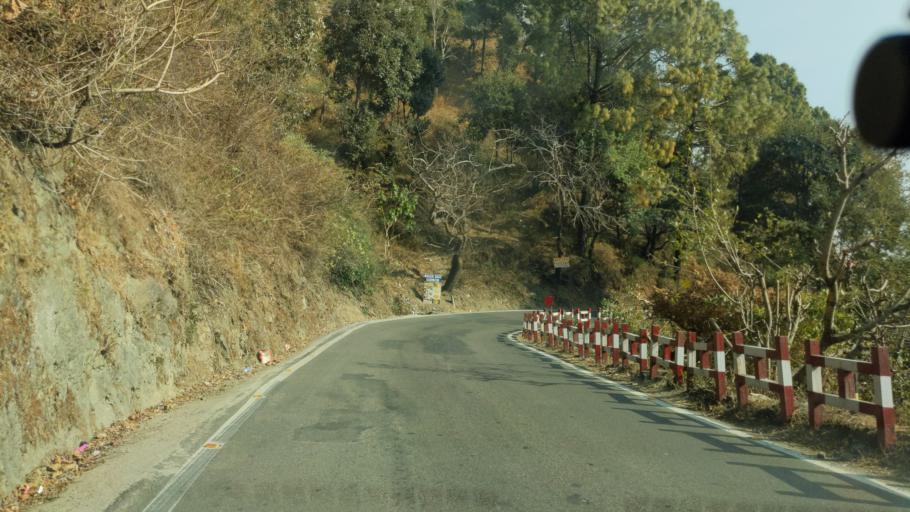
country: IN
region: Uttarakhand
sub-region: Naini Tal
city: Bhowali
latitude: 29.3805
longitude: 79.5227
